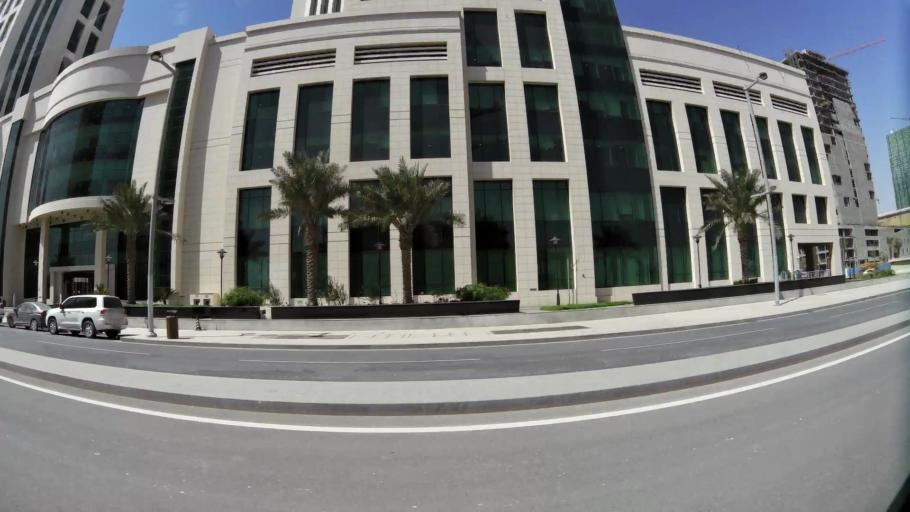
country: QA
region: Baladiyat ad Dawhah
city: Doha
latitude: 25.3939
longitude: 51.5220
